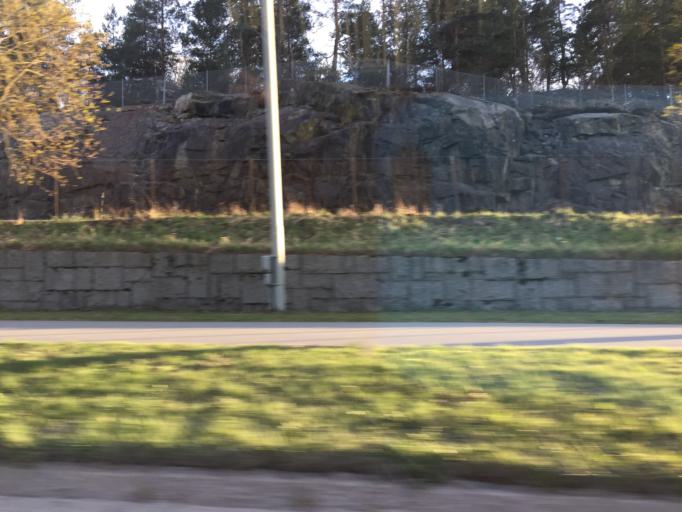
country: SE
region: Stockholm
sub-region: Stockholms Kommun
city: Bromma
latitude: 59.3453
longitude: 17.8980
